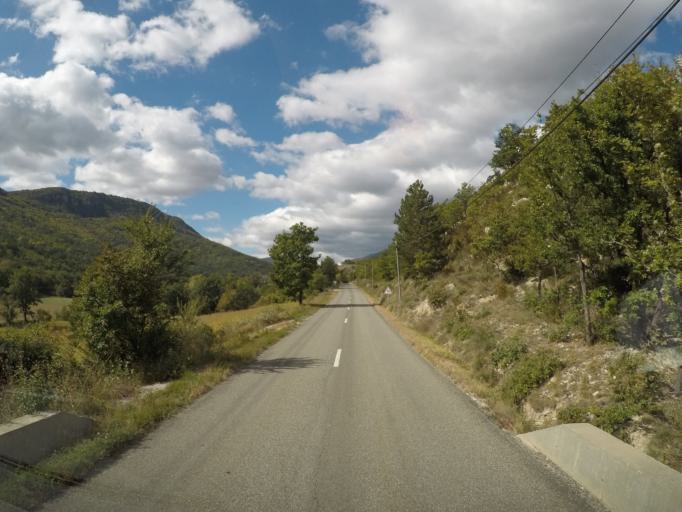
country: FR
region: Provence-Alpes-Cote d'Azur
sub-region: Departement des Hautes-Alpes
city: Laragne-Monteglin
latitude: 44.1748
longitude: 5.6881
